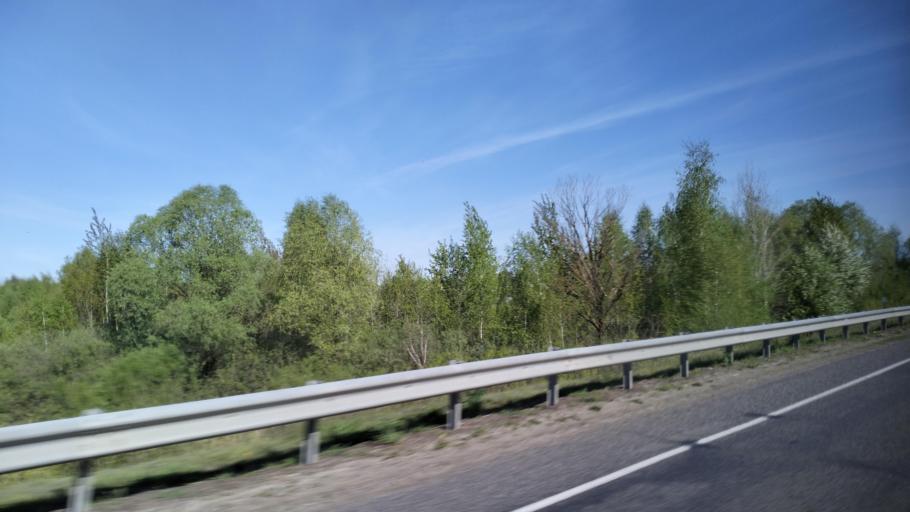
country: BY
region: Gomel
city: Turaw
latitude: 52.0949
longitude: 27.8296
